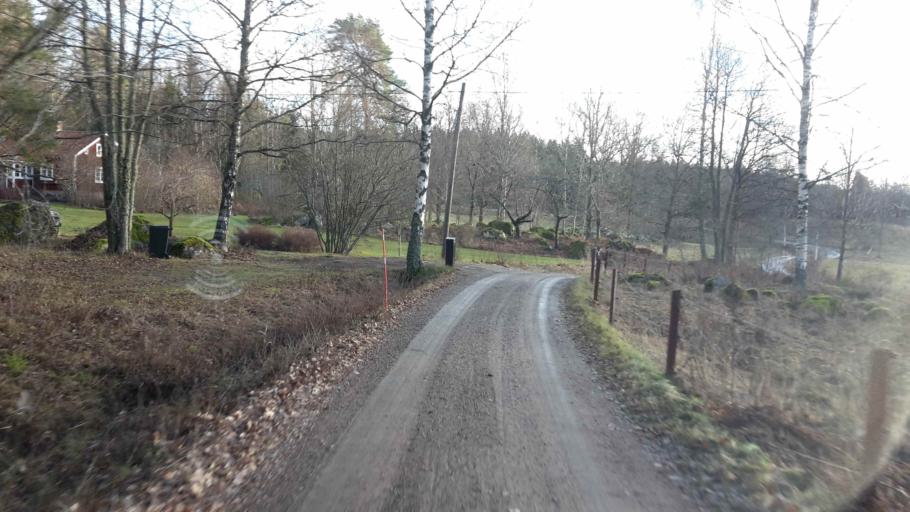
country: SE
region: OEstergoetland
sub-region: Atvidabergs Kommun
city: Atvidaberg
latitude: 58.2856
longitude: 16.0925
